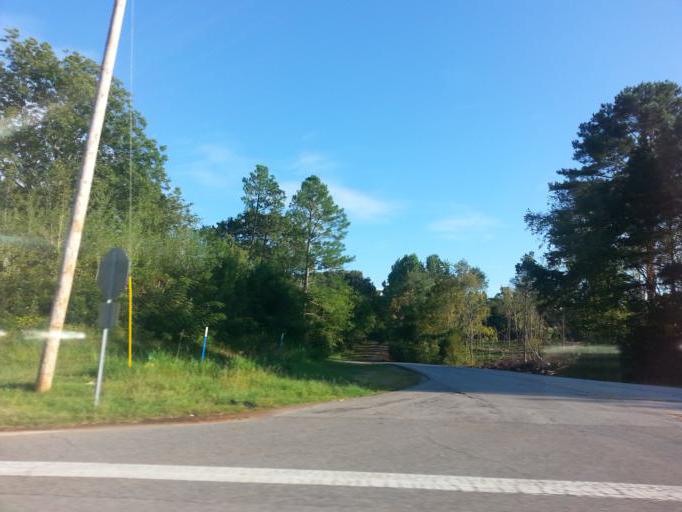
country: US
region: Alabama
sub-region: Lauderdale County
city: Killen
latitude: 34.8585
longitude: -87.5340
